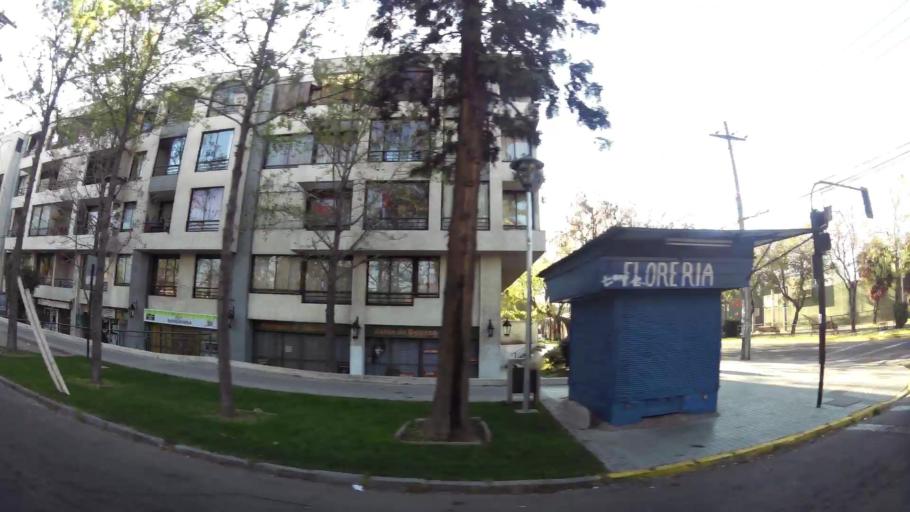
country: CL
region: Santiago Metropolitan
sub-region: Provincia de Santiago
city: Villa Presidente Frei, Nunoa, Santiago, Chile
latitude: -33.4528
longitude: -70.5652
